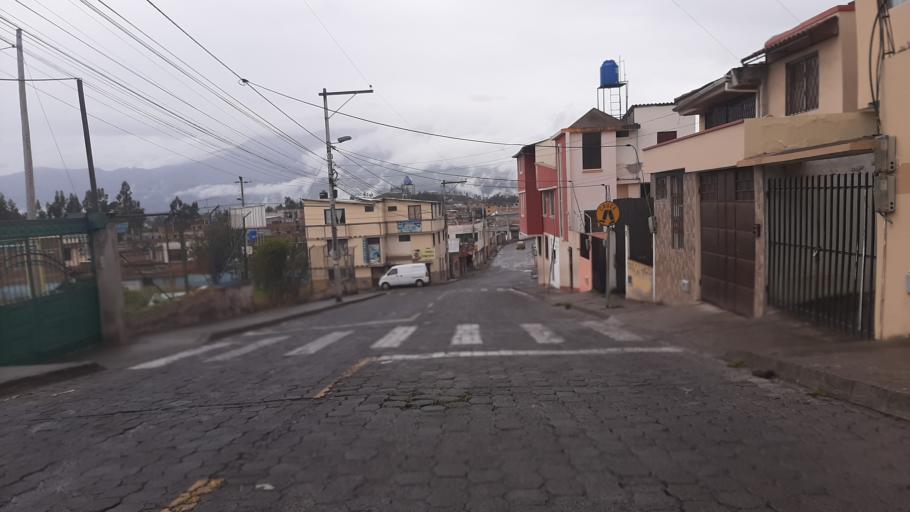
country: EC
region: Chimborazo
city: Riobamba
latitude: -1.6553
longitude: -78.6424
